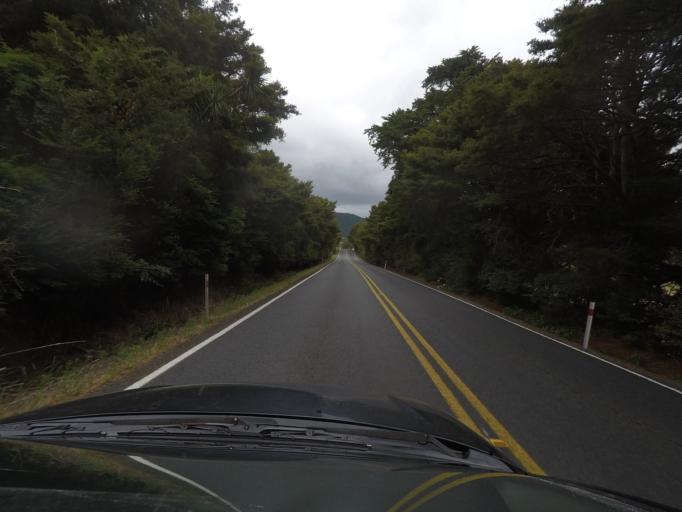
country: NZ
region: Auckland
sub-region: Auckland
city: Wellsford
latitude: -36.2870
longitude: 174.6308
